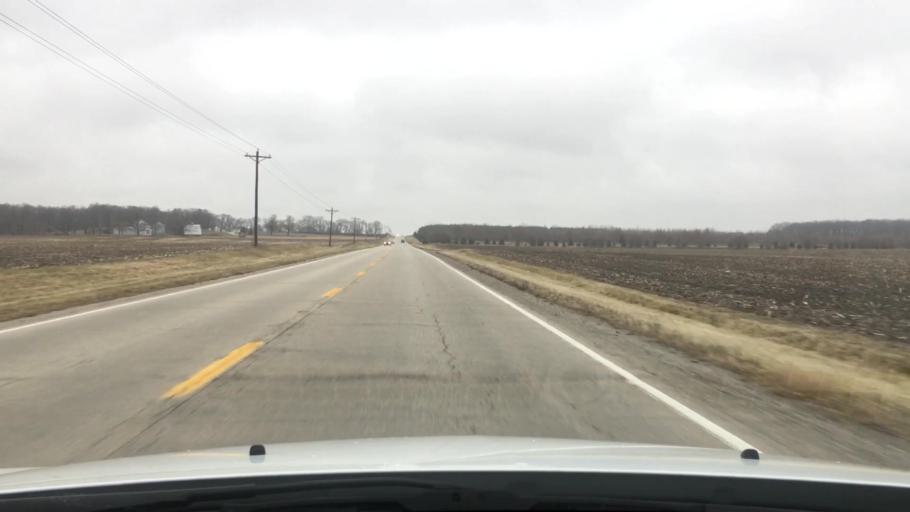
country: US
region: Illinois
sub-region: Iroquois County
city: Watseka
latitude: 40.8913
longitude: -87.6774
